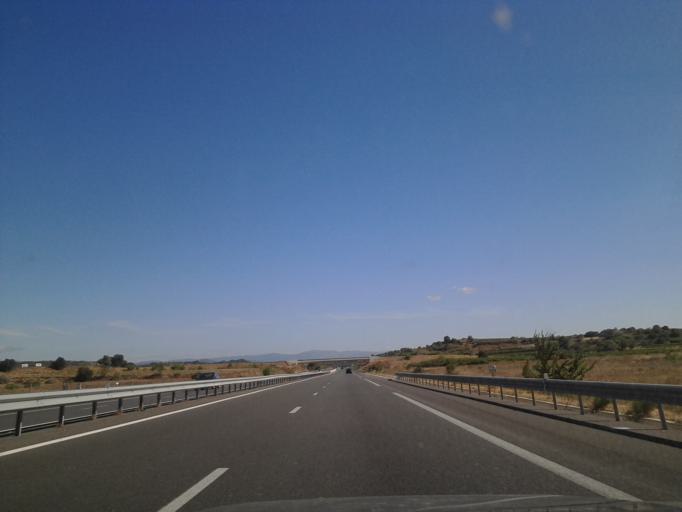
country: FR
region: Languedoc-Roussillon
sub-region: Departement de l'Herault
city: Tourbes
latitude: 43.4244
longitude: 3.3889
